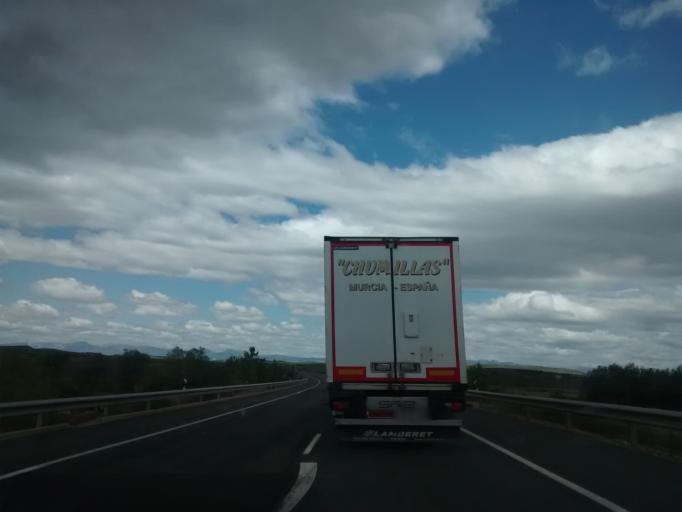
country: ES
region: La Rioja
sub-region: Provincia de La Rioja
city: Ausejo
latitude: 42.3531
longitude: -2.1822
